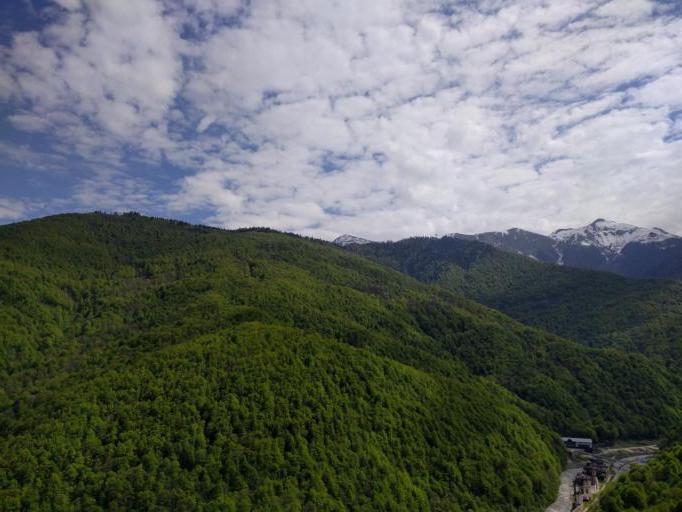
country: RU
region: Krasnodarskiy
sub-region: Sochi City
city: Krasnaya Polyana
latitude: 43.6691
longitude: 40.3025
